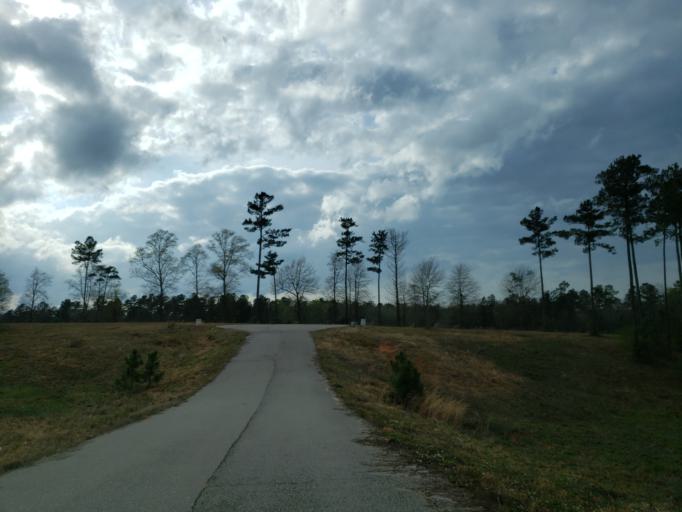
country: US
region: Mississippi
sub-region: Jones County
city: Ellisville
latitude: 31.5596
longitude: -89.2558
